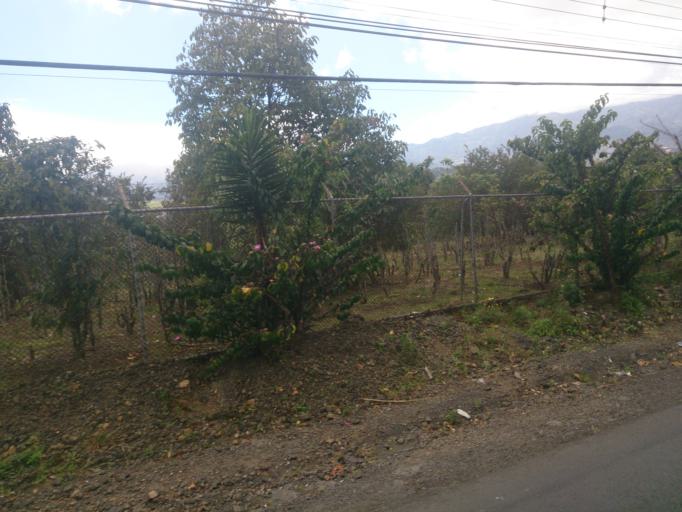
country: CR
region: San Jose
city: Granadilla
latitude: 9.9269
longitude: -84.0173
